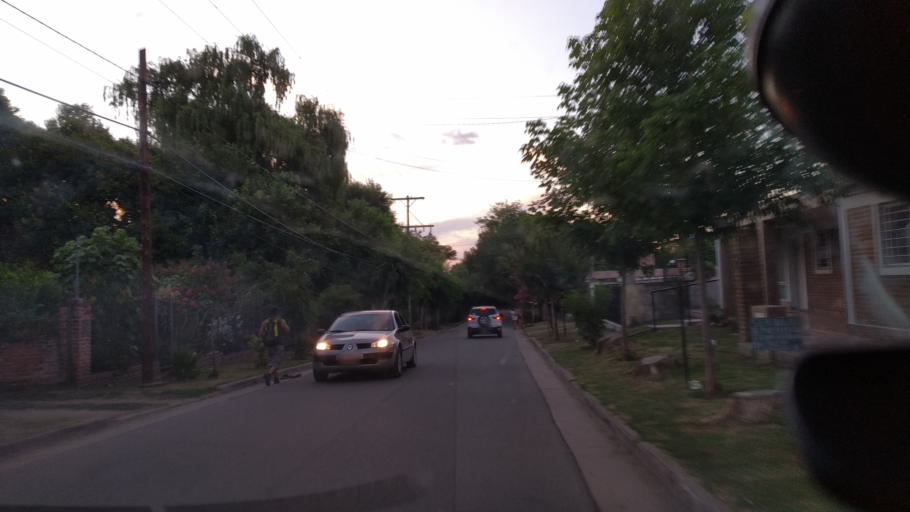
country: AR
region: Cordoba
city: Villa Las Rosas
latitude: -31.9456
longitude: -65.0559
